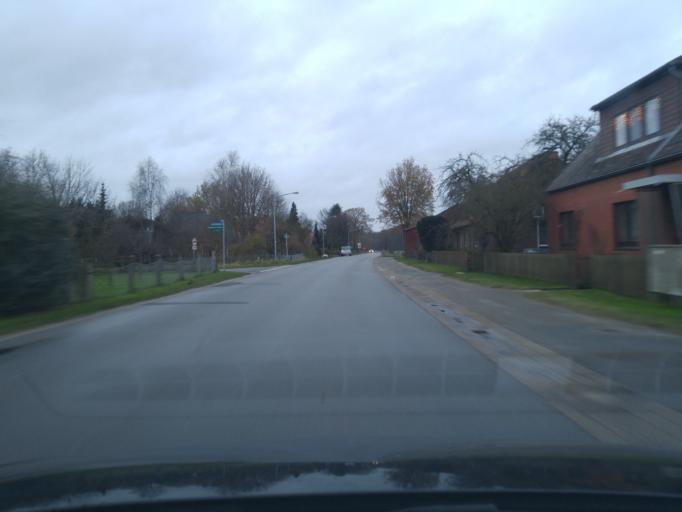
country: DE
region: Lower Saxony
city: Scharnebeck
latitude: 53.2984
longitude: 10.5055
